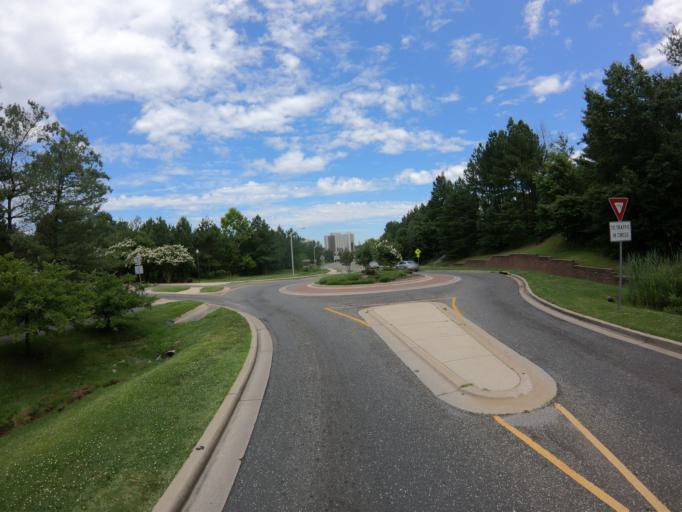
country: US
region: Maryland
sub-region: Prince George's County
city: New Carrollton
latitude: 38.9857
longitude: -76.8759
